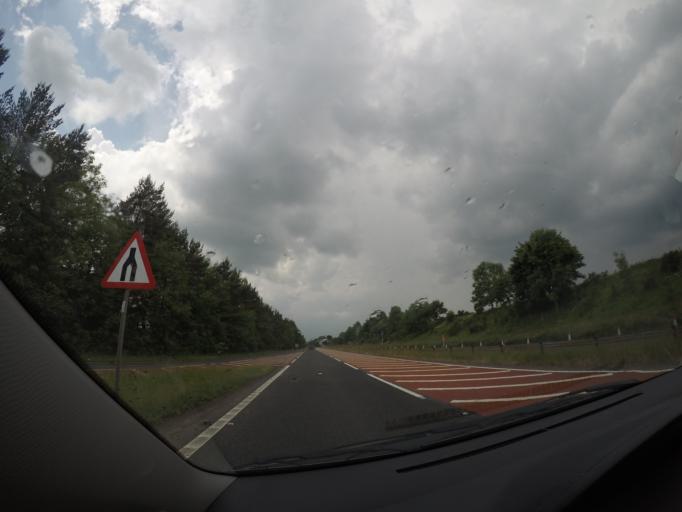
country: GB
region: England
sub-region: Cumbria
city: Appleby-in-Westmorland
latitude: 54.5887
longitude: -2.5042
